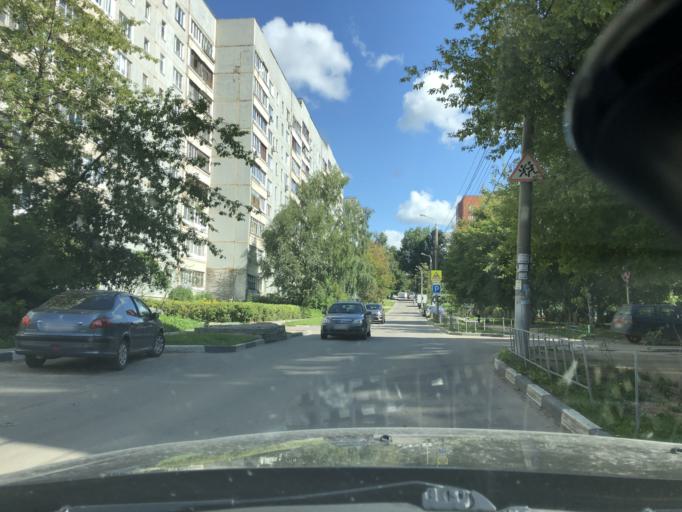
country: RU
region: Tula
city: Tula
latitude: 54.2097
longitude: 37.6241
